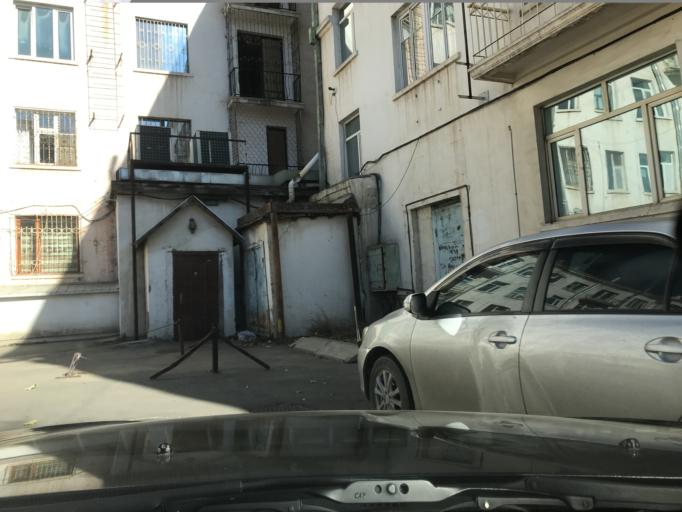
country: MN
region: Ulaanbaatar
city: Ulaanbaatar
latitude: 47.9195
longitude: 106.9147
